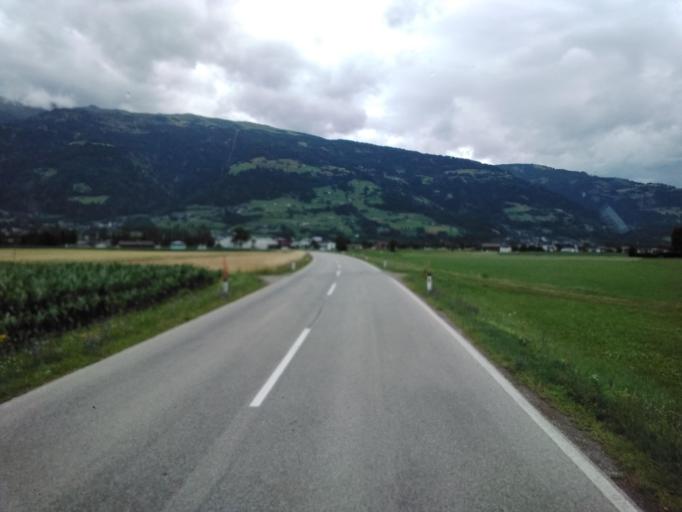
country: AT
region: Tyrol
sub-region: Politischer Bezirk Lienz
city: Amlach
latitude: 46.8165
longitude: 12.7647
